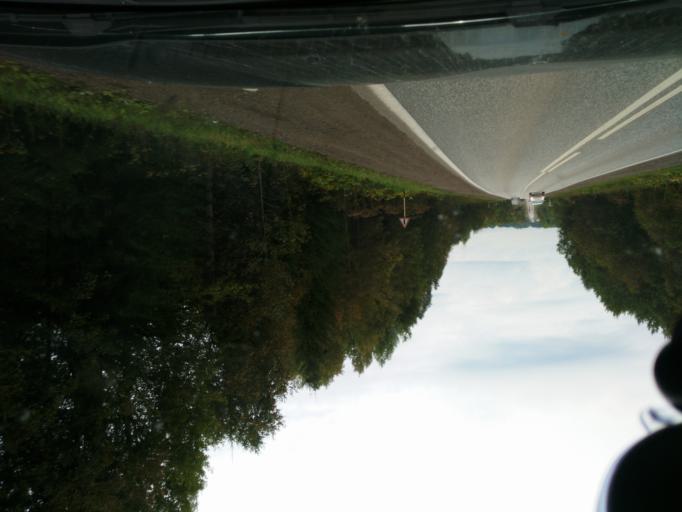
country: RU
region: Perm
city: Chernushka
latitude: 56.6005
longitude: 56.1604
